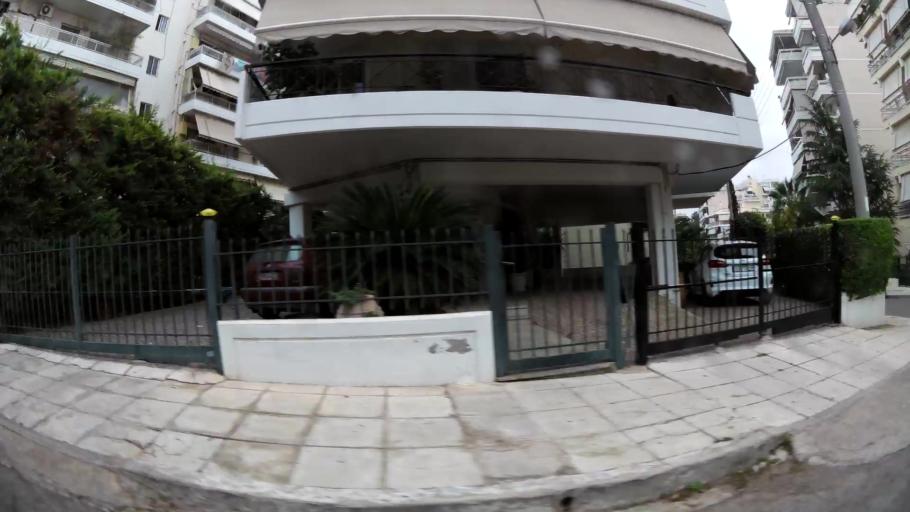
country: GR
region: Attica
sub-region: Nomarchia Athinas
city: Palaio Faliro
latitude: 37.9193
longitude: 23.7088
